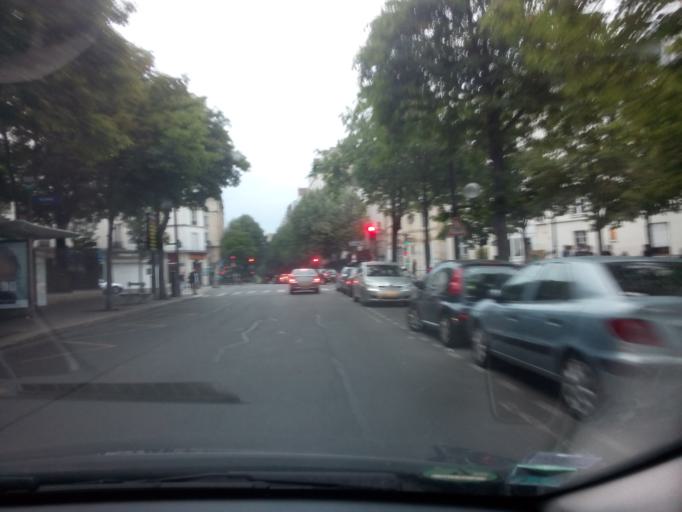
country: FR
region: Ile-de-France
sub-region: Departement du Val-de-Marne
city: Le Kremlin-Bicetre
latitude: 48.8277
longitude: 2.3523
